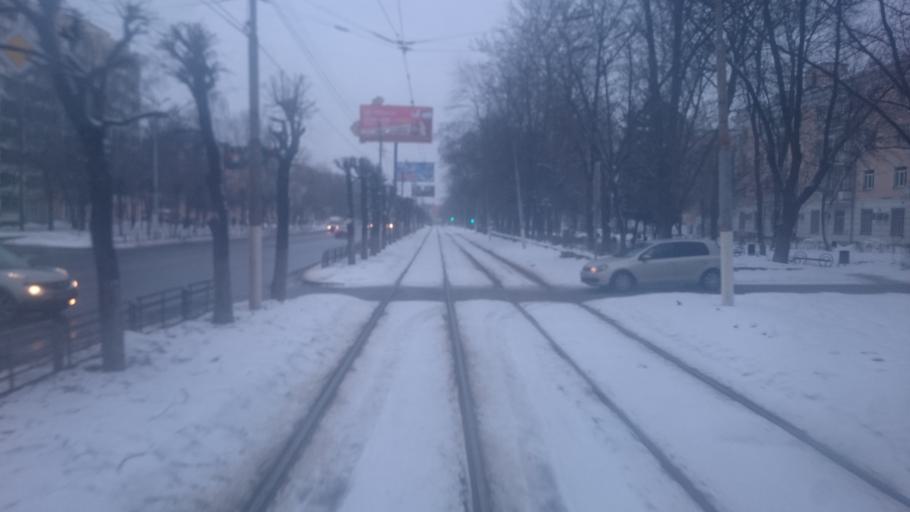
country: RU
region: Tverskaya
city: Tver
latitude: 56.8419
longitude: 35.8998
